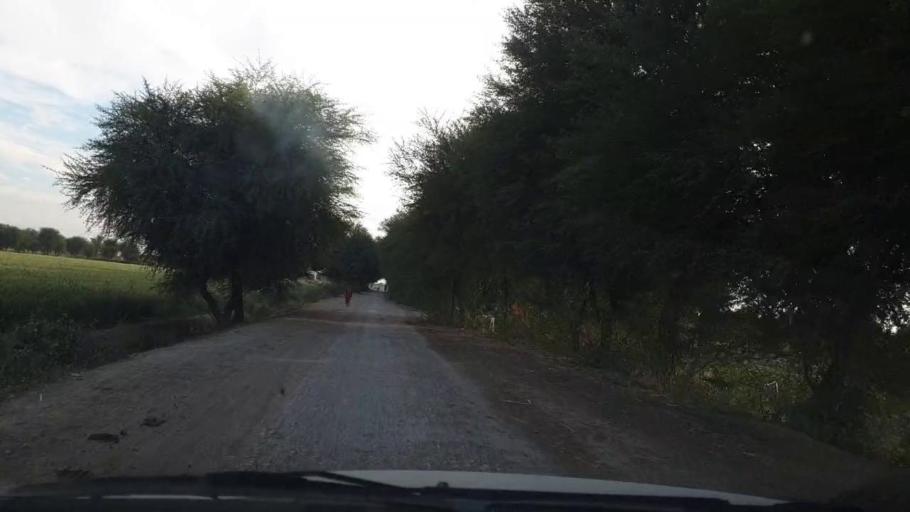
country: PK
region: Sindh
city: Pithoro
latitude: 25.6457
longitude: 69.2762
